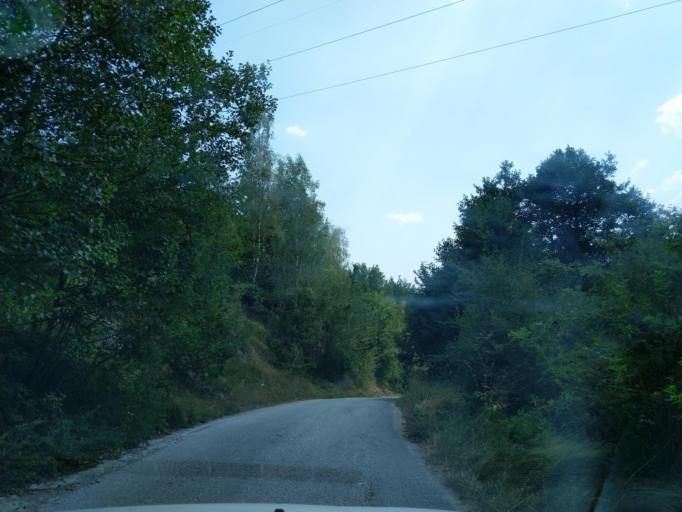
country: RS
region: Central Serbia
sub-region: Zlatiborski Okrug
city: Prijepolje
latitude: 43.3323
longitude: 19.5688
